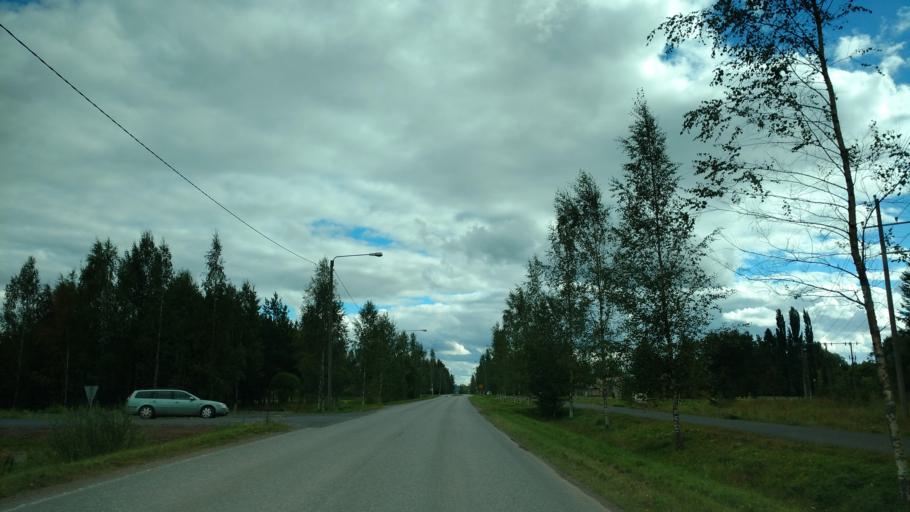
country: FI
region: Haeme
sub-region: Forssa
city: Ypaejae
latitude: 60.8082
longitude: 23.2718
